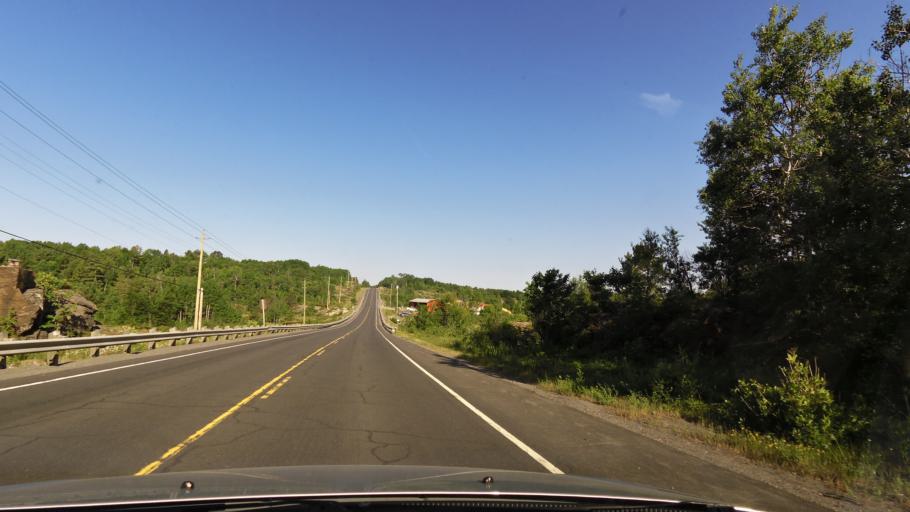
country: CA
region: Ontario
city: Greater Sudbury
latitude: 46.1048
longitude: -80.6373
